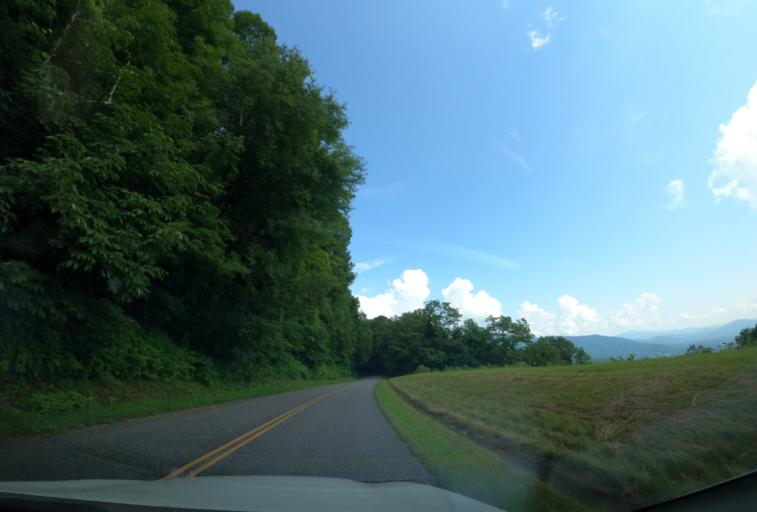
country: US
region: North Carolina
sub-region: Haywood County
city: Hazelwood
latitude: 35.4371
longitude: -83.0485
